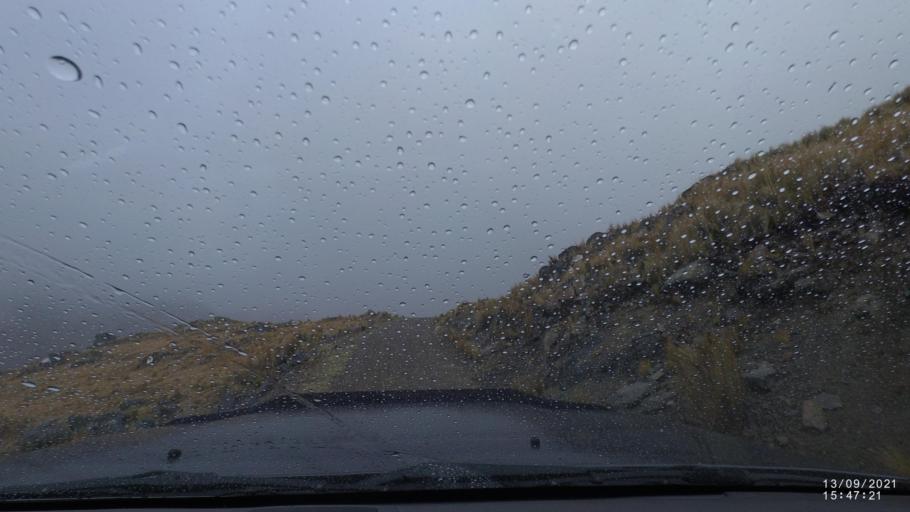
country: BO
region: Cochabamba
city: Colomi
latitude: -17.3133
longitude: -65.7187
